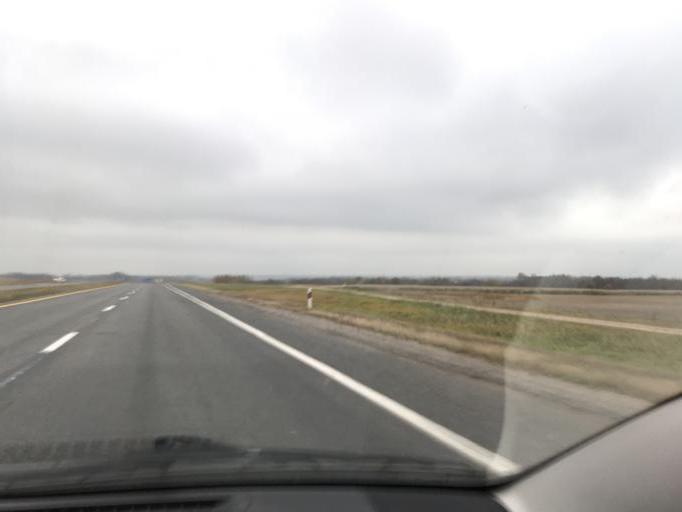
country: BY
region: Vitebsk
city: Vitebsk
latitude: 55.1557
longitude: 30.0815
